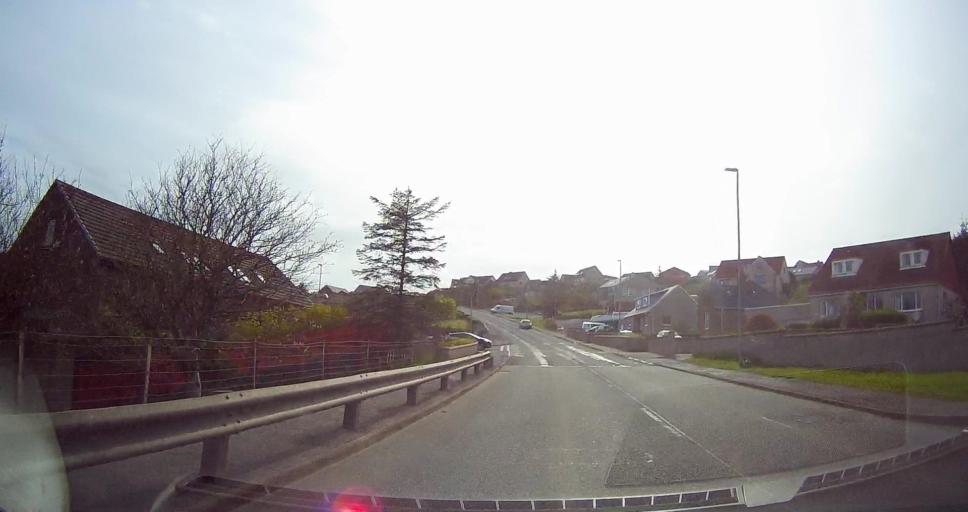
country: GB
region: Scotland
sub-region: Shetland Islands
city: Lerwick
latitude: 60.1440
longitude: -1.1768
